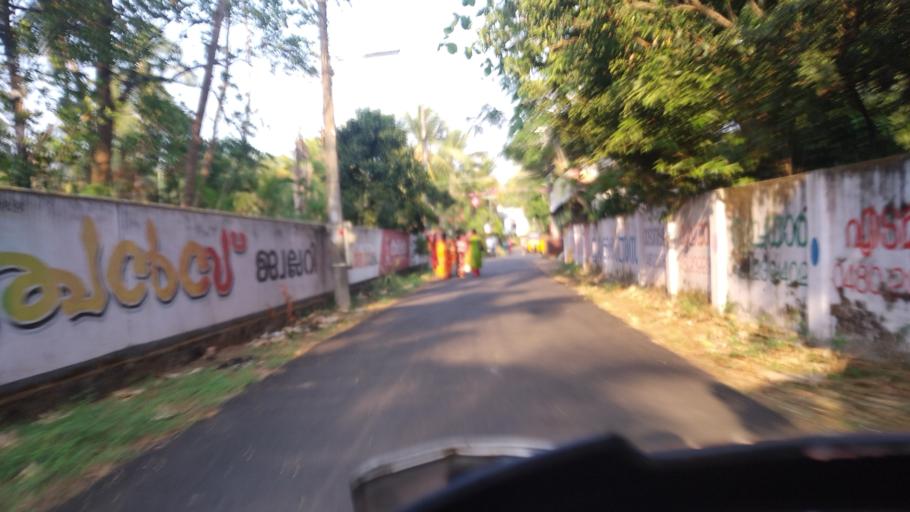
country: IN
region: Kerala
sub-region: Thrissur District
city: Thanniyam
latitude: 10.4388
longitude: 76.0787
